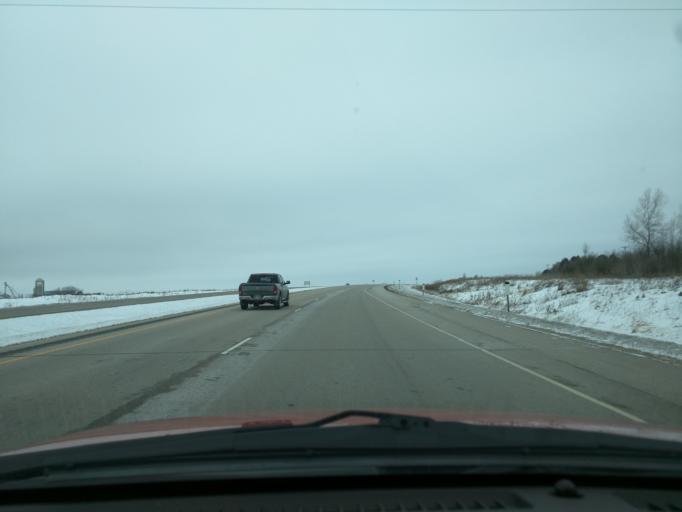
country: US
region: Minnesota
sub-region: Winona County
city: Winona
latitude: 43.9161
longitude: -91.6029
